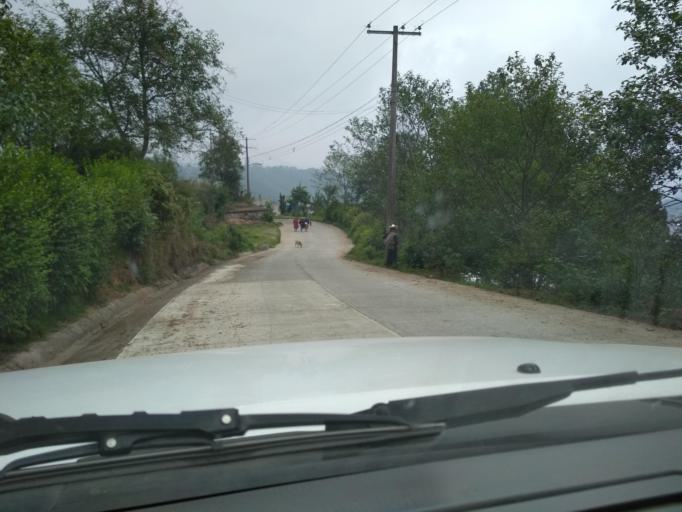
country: MX
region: Veracruz
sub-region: La Perla
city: Chilapa
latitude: 18.9895
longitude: -97.1563
